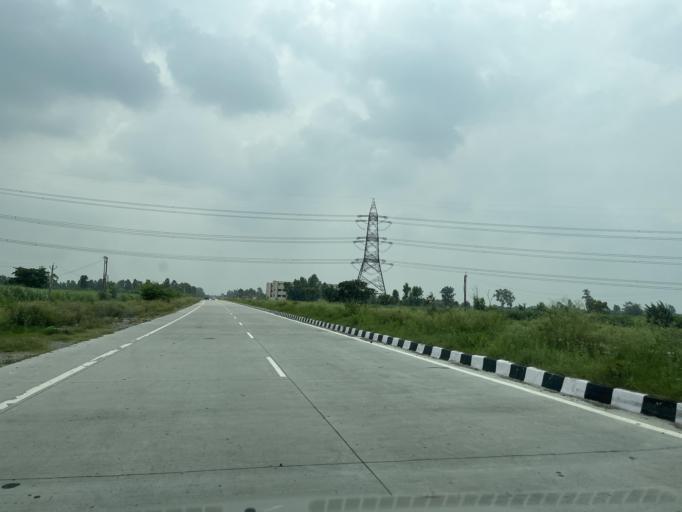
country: IN
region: Uttar Pradesh
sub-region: Bijnor
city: Najibabad
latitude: 29.5646
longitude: 78.3388
